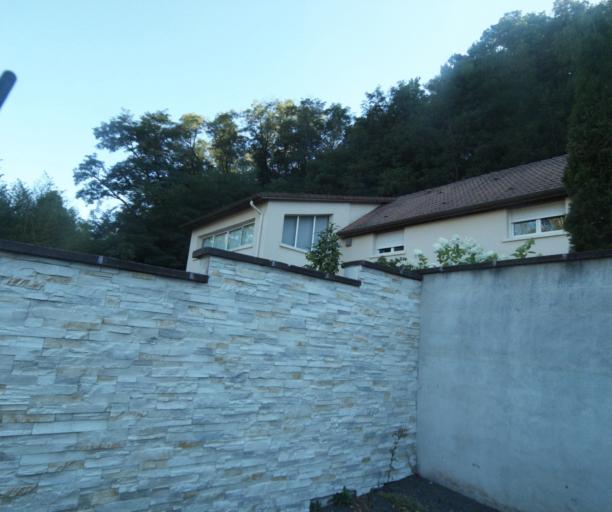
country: FR
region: Lorraine
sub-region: Departement des Vosges
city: Epinal
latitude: 48.1683
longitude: 6.4568
